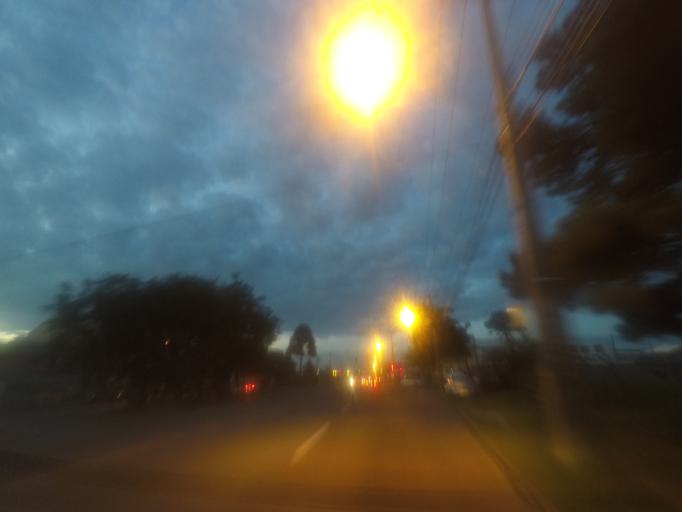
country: BR
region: Parana
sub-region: Pinhais
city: Pinhais
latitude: -25.3963
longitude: -49.1891
